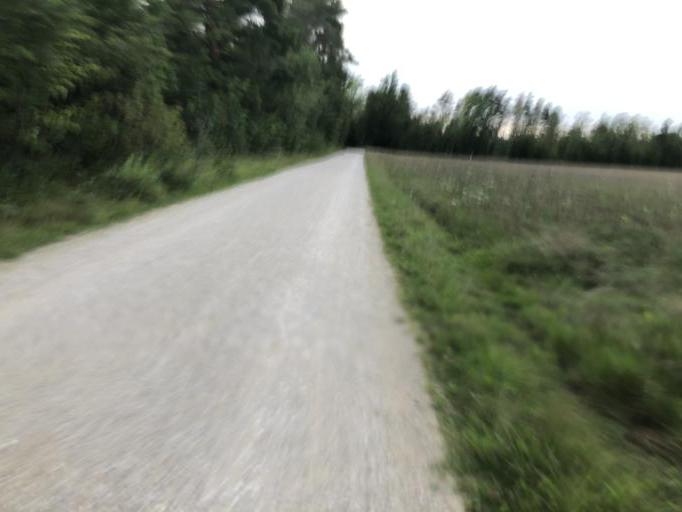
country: DE
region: Bavaria
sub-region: Regierungsbezirk Mittelfranken
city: Uttenreuth
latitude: 49.5882
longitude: 11.0760
